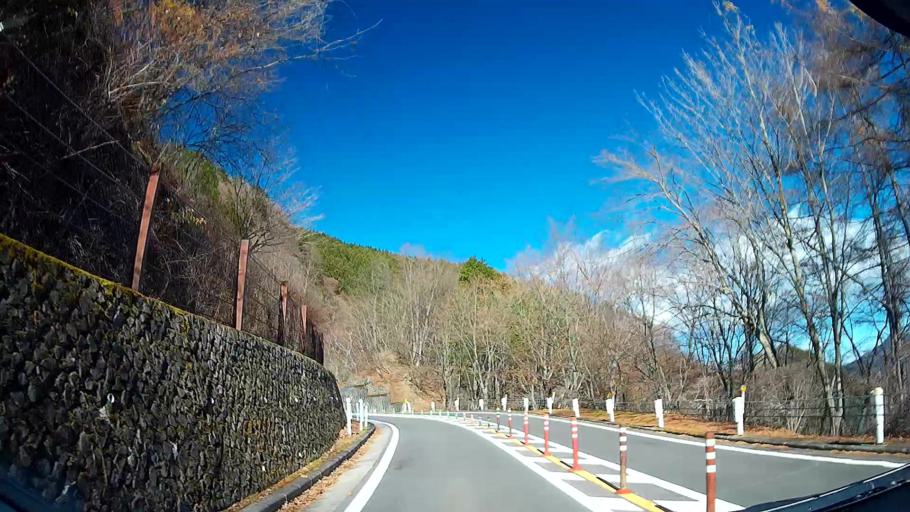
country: JP
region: Yamanashi
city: Uenohara
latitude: 35.7404
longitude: 139.0426
